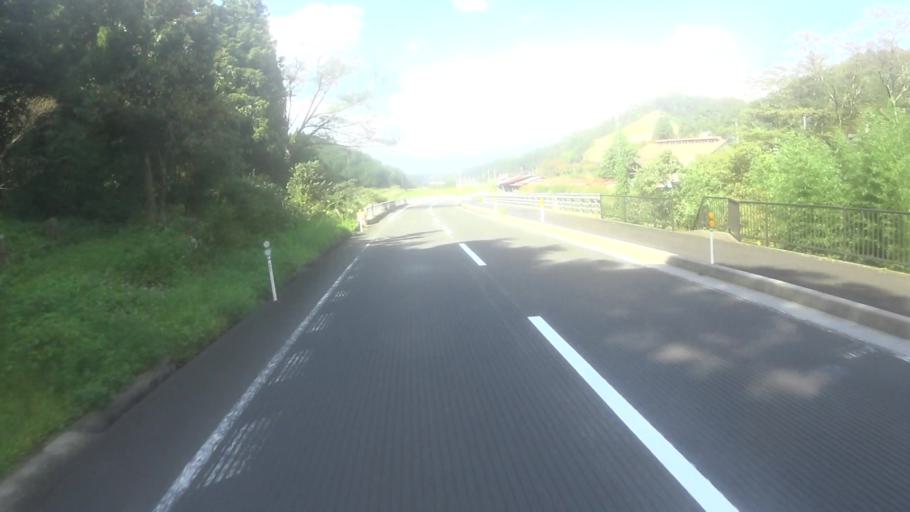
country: JP
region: Kyoto
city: Miyazu
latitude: 35.6481
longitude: 135.1249
